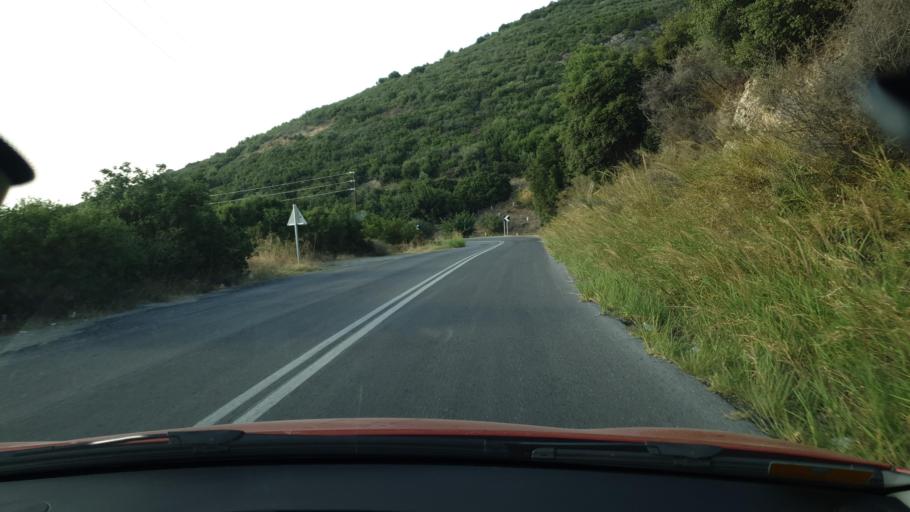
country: GR
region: Thessaly
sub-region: Nomos Magnisias
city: Pteleos
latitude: 39.0641
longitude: 22.9274
